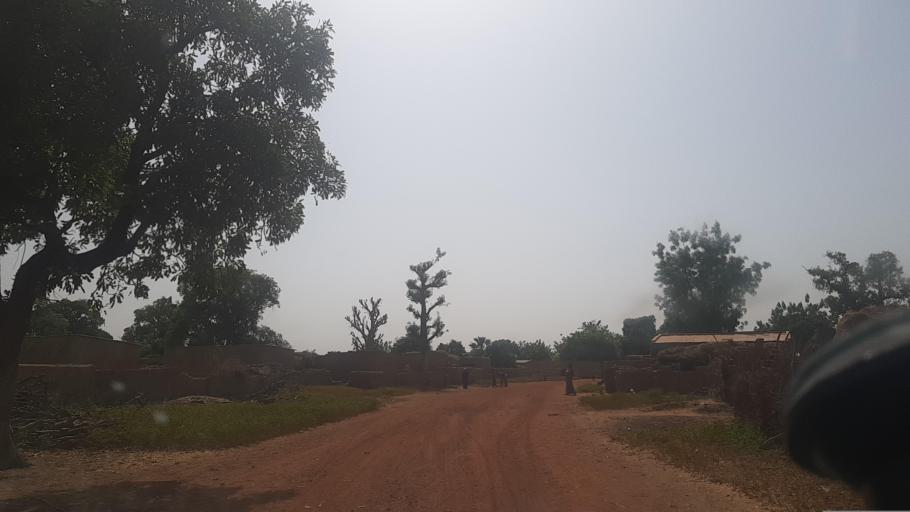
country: ML
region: Segou
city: Baroueli
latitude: 13.0136
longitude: -6.4230
